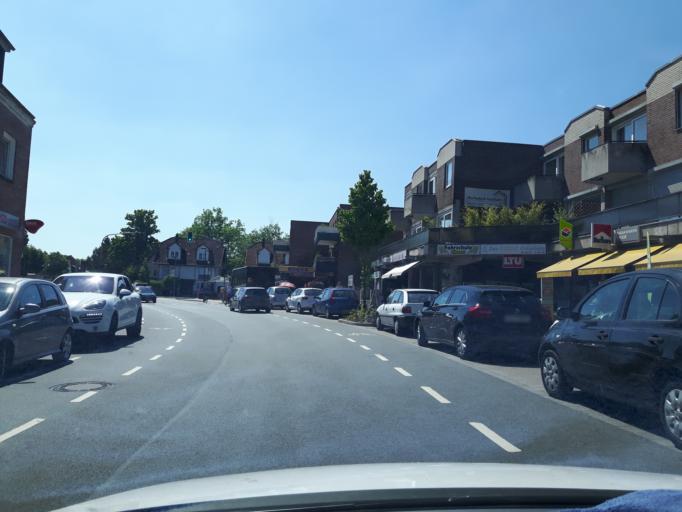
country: DE
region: North Rhine-Westphalia
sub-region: Regierungsbezirk Dusseldorf
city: Ratingen
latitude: 51.3328
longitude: 6.7890
